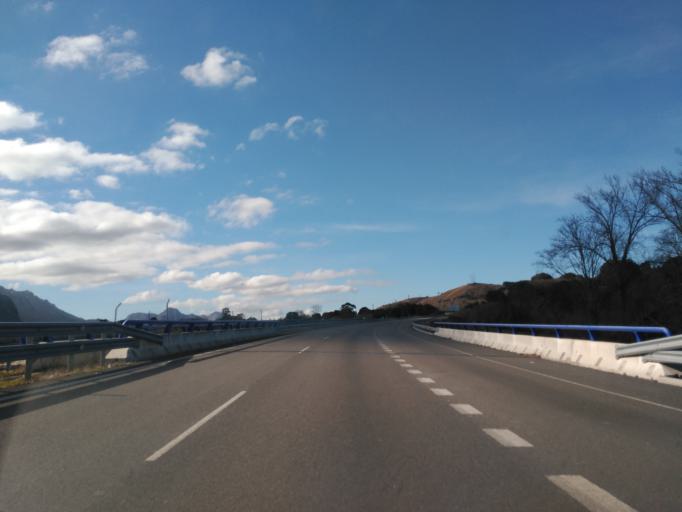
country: ES
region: Asturias
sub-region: Province of Asturias
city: Llanes
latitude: 43.3987
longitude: -4.7159
